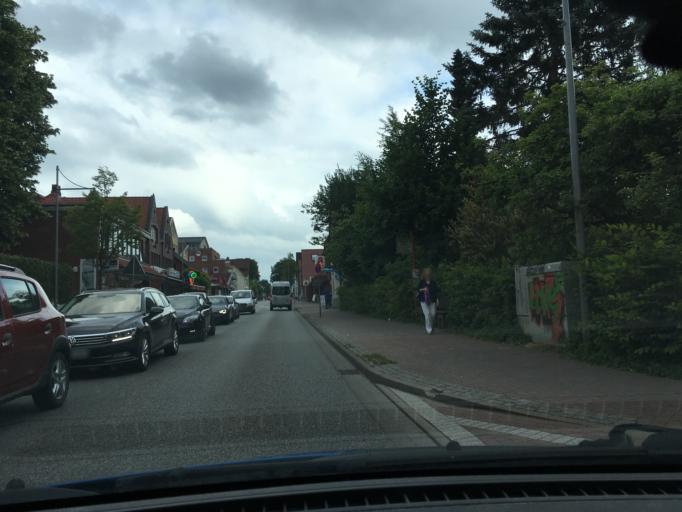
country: DE
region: Lower Saxony
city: Tostedt
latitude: 53.2805
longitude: 9.7129
